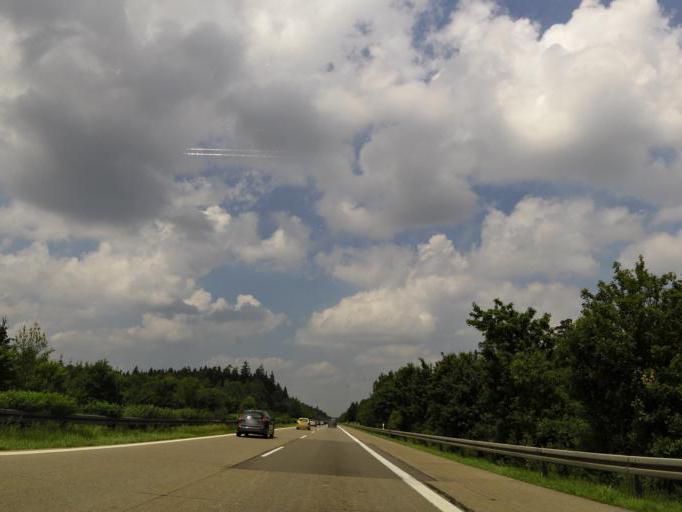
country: DE
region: Baden-Wuerttemberg
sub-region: Regierungsbezirk Stuttgart
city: Ellenberg
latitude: 49.0327
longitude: 10.1901
